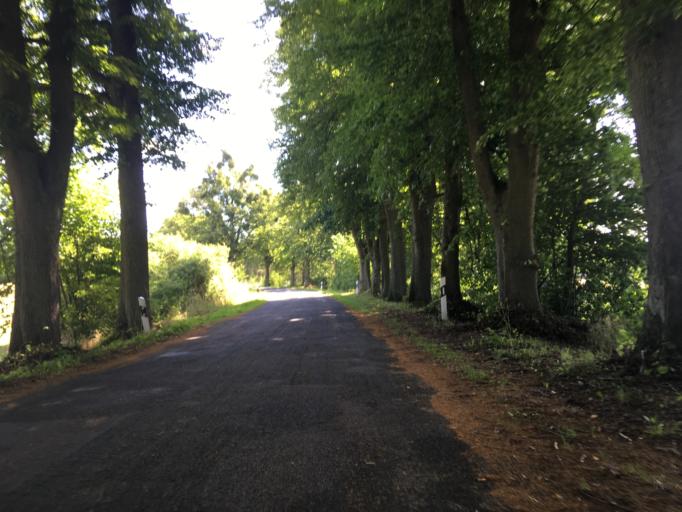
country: DE
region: Brandenburg
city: Templin
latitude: 53.1774
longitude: 13.5254
